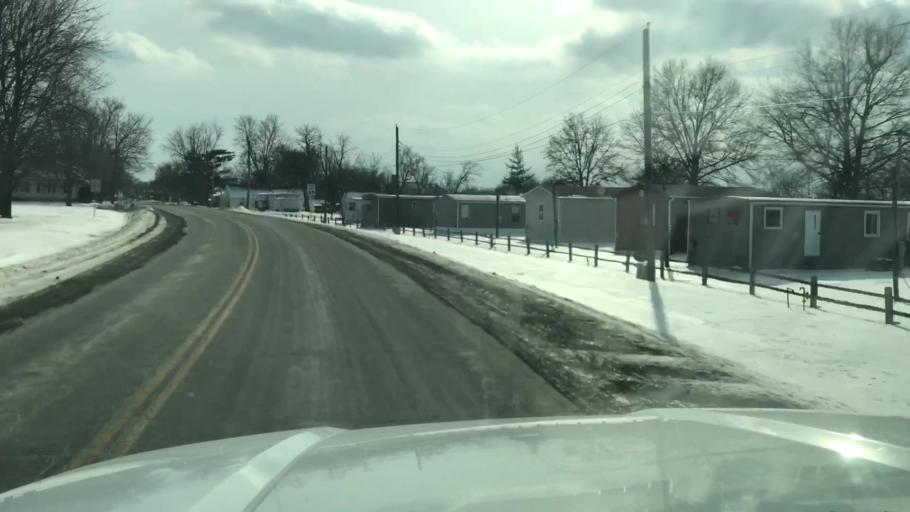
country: US
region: Missouri
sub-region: Gentry County
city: Stanberry
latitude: 40.3567
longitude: -94.6729
